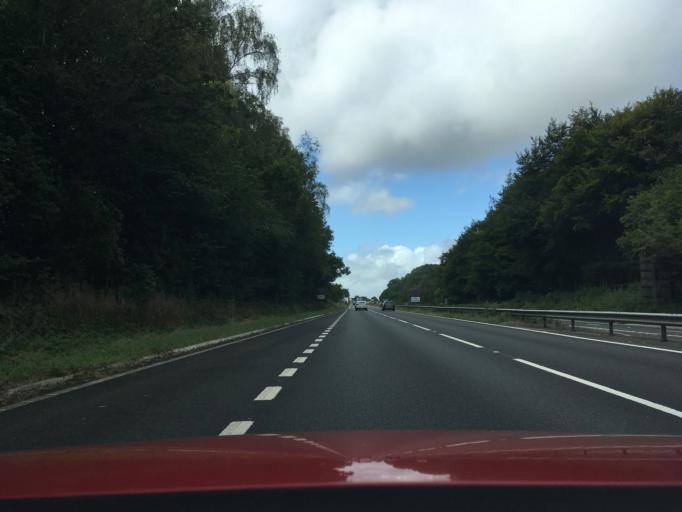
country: GB
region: England
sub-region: Hampshire
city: Overton
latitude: 51.1980
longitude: -1.2135
